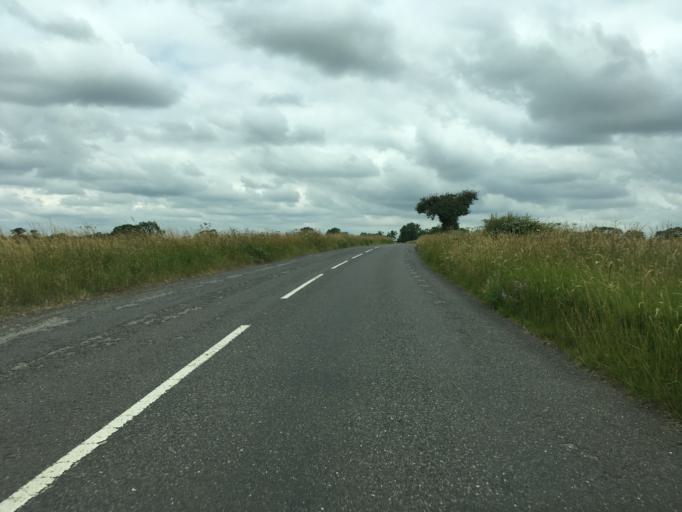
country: GB
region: England
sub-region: Oxfordshire
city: Charlbury
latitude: 51.9107
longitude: -1.4897
